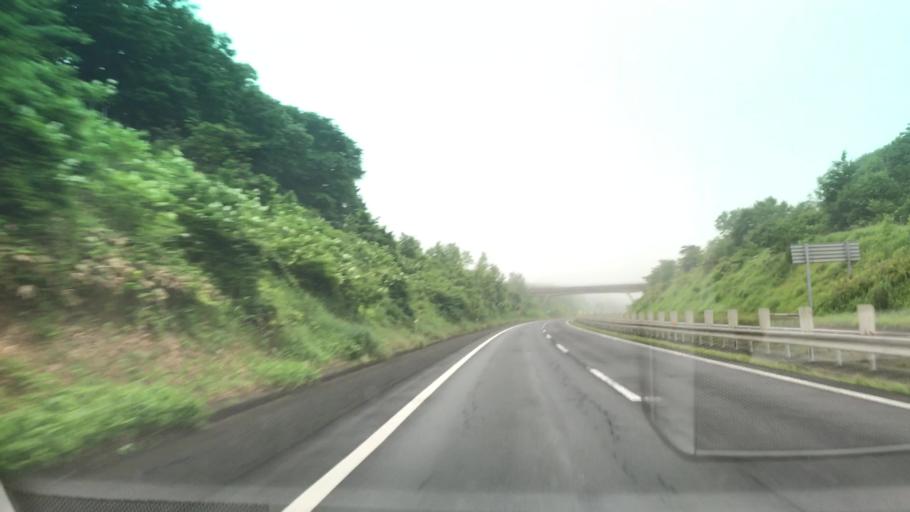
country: JP
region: Hokkaido
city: Muroran
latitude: 42.4479
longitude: 141.1564
